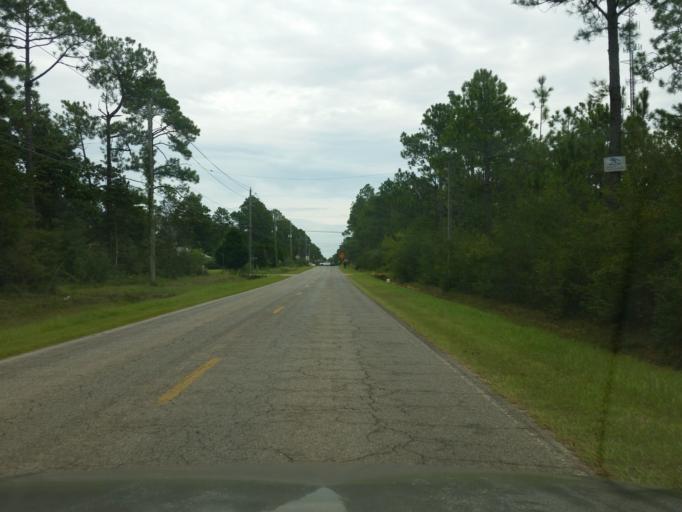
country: US
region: Florida
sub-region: Santa Rosa County
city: Bagdad
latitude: 30.5442
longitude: -87.0906
